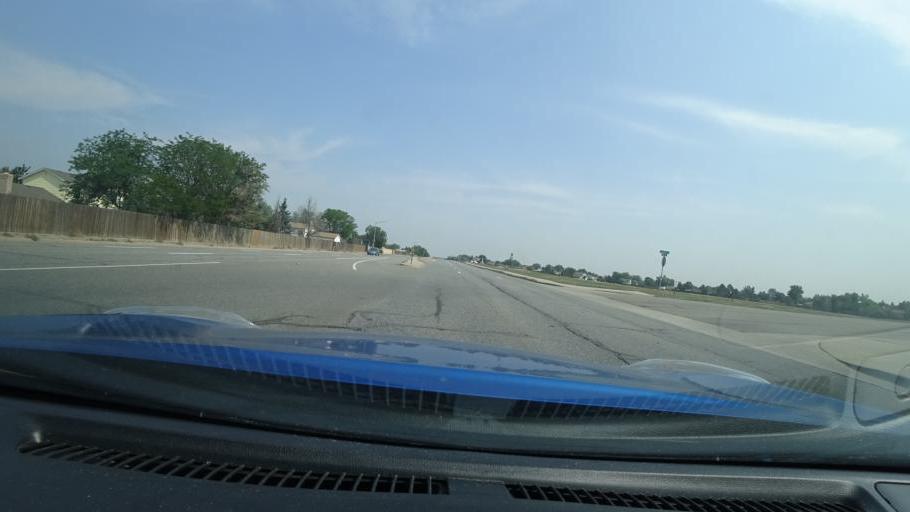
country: US
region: Colorado
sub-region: Adams County
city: Aurora
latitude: 39.6844
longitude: -104.7723
